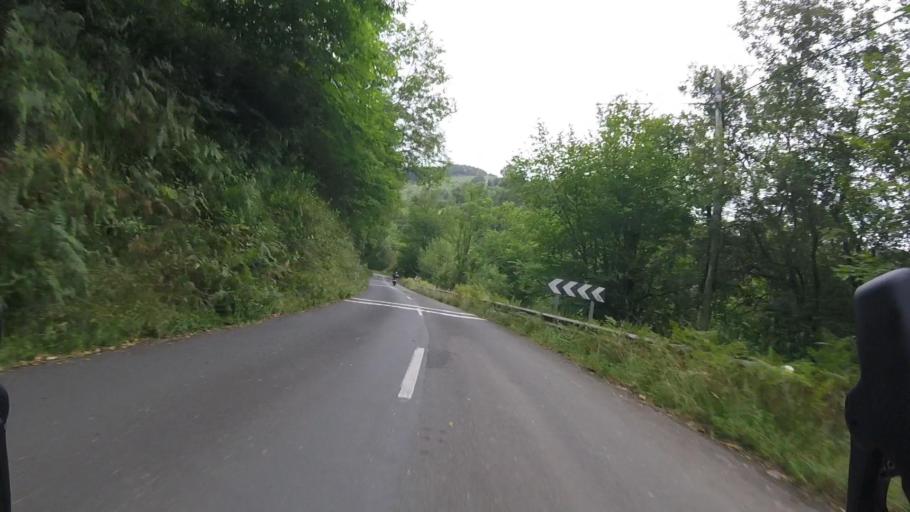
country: ES
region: Basque Country
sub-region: Provincia de Guipuzcoa
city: Irun
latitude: 43.2815
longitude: -1.8204
